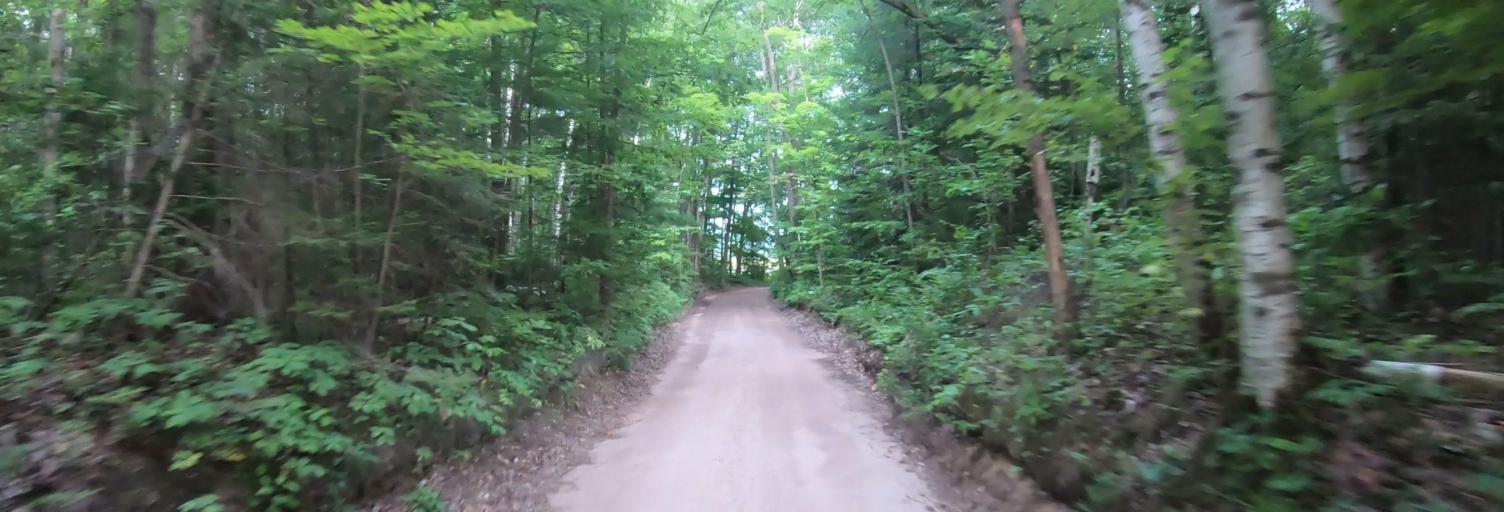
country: US
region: Michigan
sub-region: Mackinac County
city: Saint Ignace
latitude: 45.7635
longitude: -84.7673
